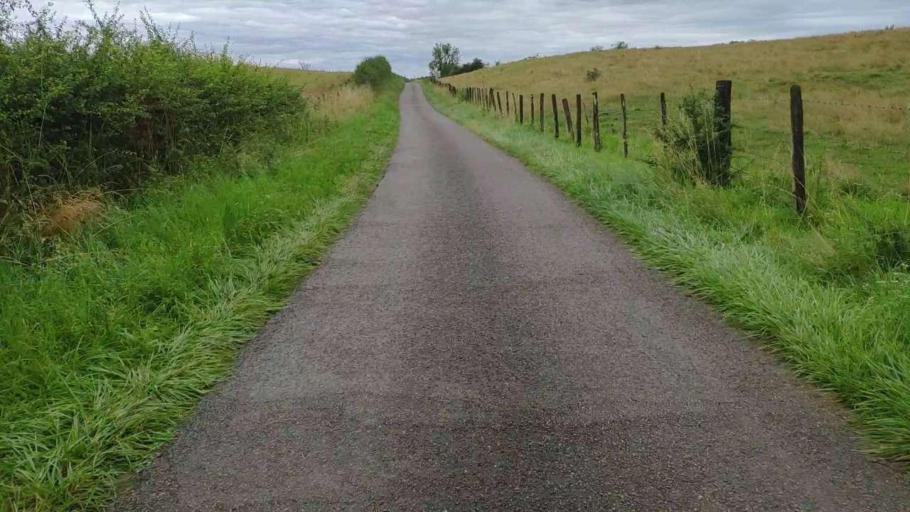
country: FR
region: Franche-Comte
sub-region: Departement du Jura
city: Perrigny
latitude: 46.7757
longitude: 5.5890
